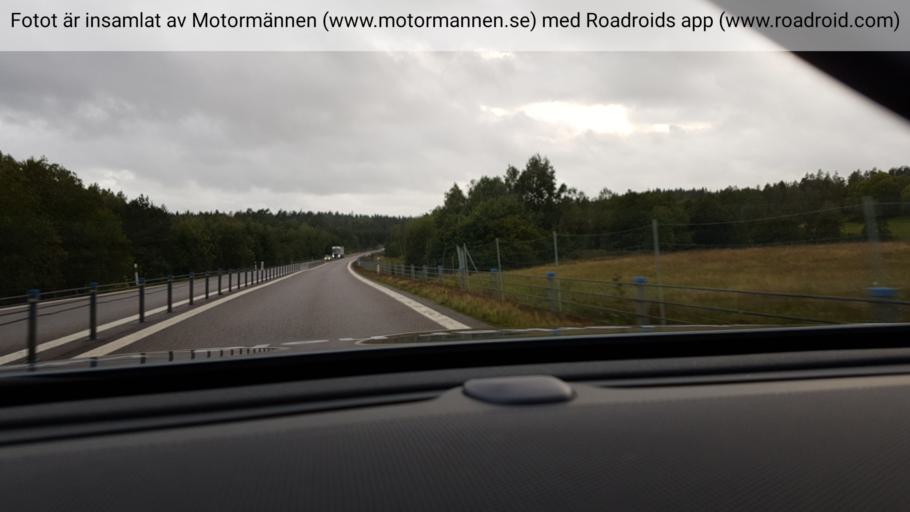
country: SE
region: Vaestra Goetaland
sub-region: Uddevalla Kommun
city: Uddevalla
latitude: 58.3298
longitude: 11.9724
